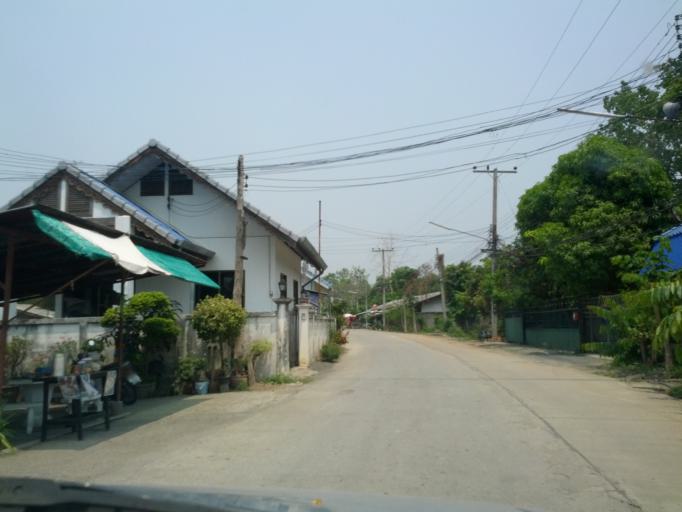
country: TH
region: Chiang Mai
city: San Sai
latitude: 18.8604
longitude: 99.1021
